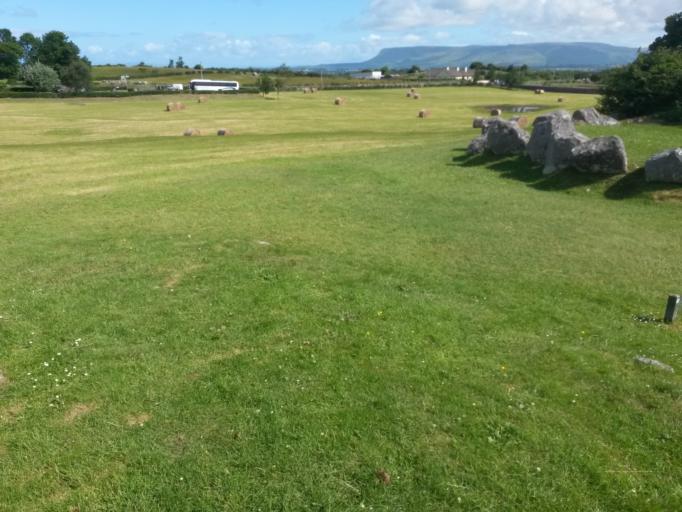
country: IE
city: Ballisodare
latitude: 54.2497
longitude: -8.5184
